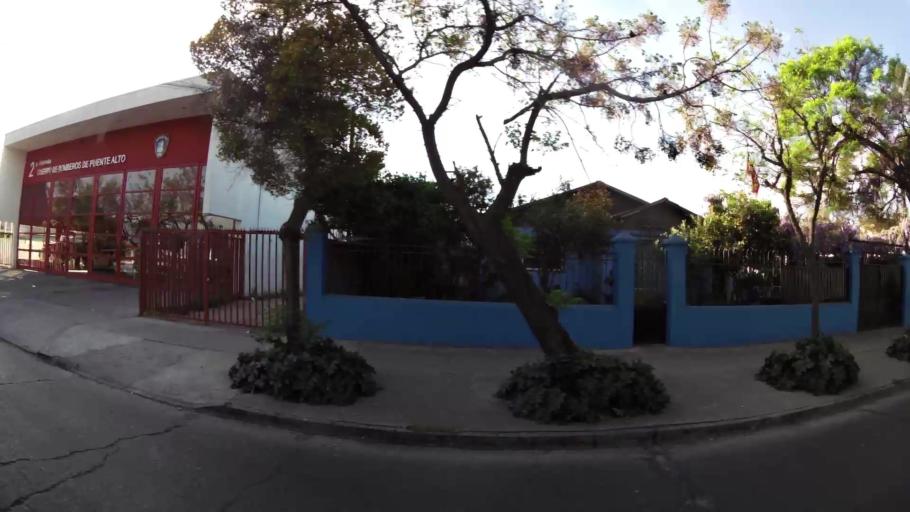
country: CL
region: Santiago Metropolitan
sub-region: Provincia de Cordillera
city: Puente Alto
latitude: -33.6066
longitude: -70.5813
